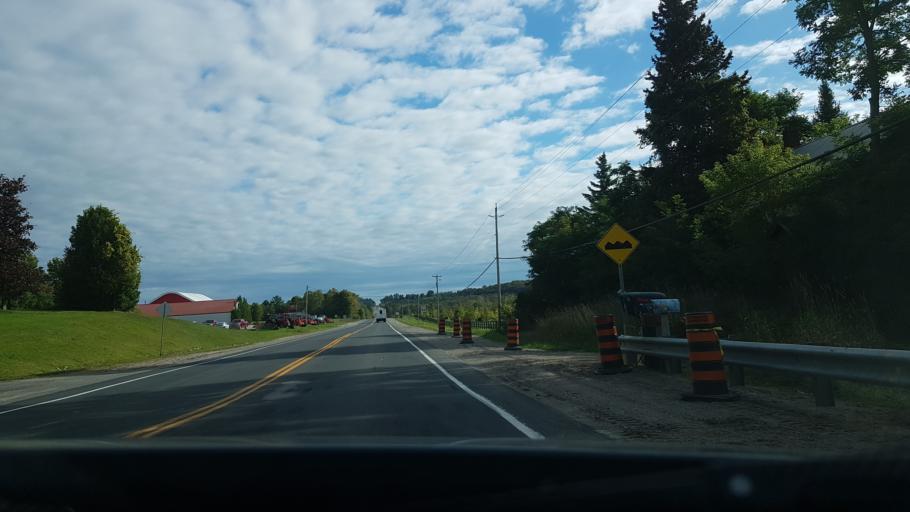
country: CA
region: Ontario
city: Orillia
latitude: 44.5990
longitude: -79.5628
